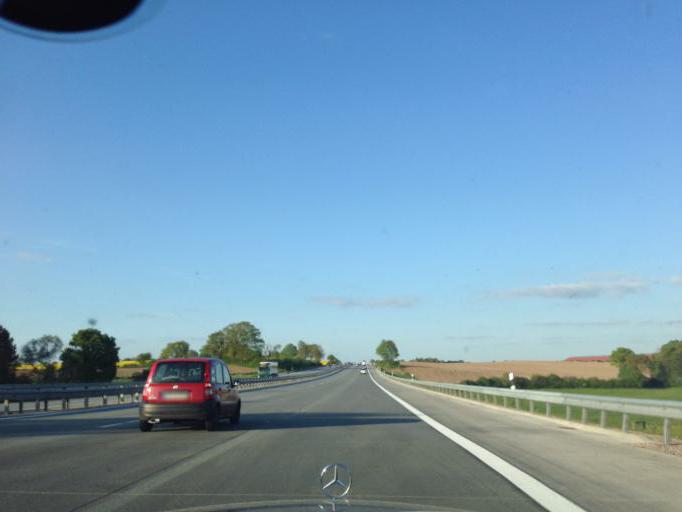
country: DE
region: Schleswig-Holstein
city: Meddewade
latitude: 53.7929
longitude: 10.4312
